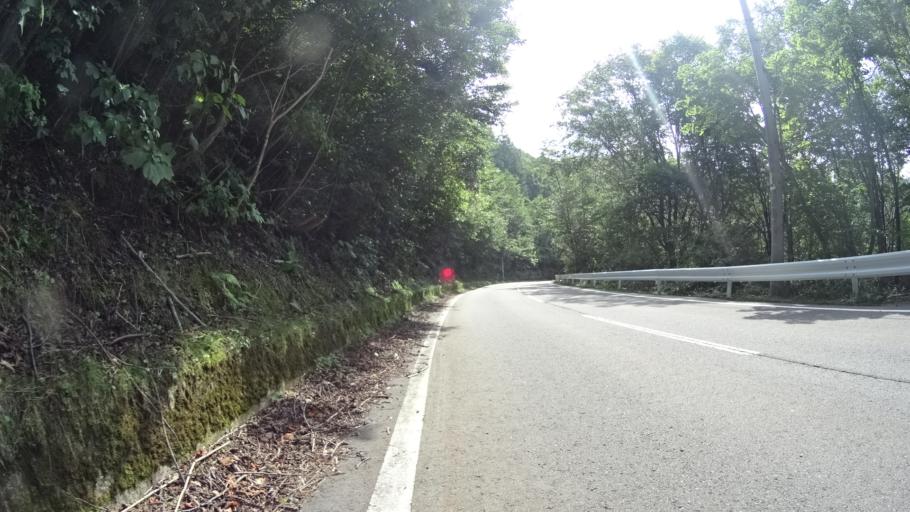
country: JP
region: Nagano
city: Saku
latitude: 36.0533
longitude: 138.4017
